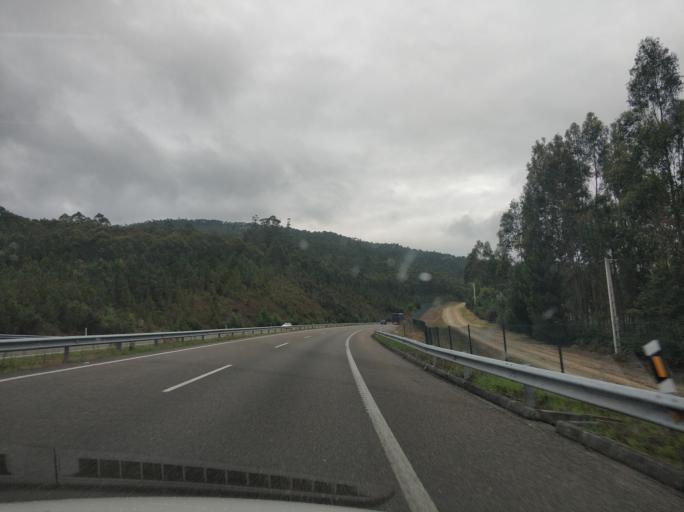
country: ES
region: Galicia
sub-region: Provincia de Lugo
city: Ribadeo
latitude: 43.5319
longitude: -7.0989
